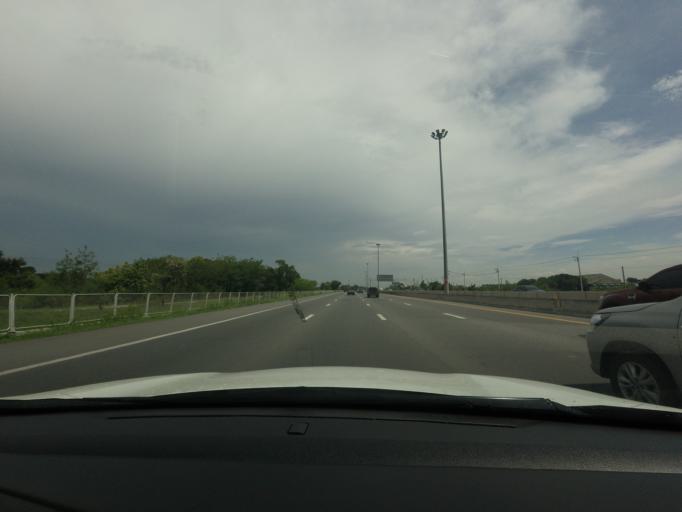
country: TH
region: Pathum Thani
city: Thanyaburi
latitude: 14.0539
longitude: 100.6980
